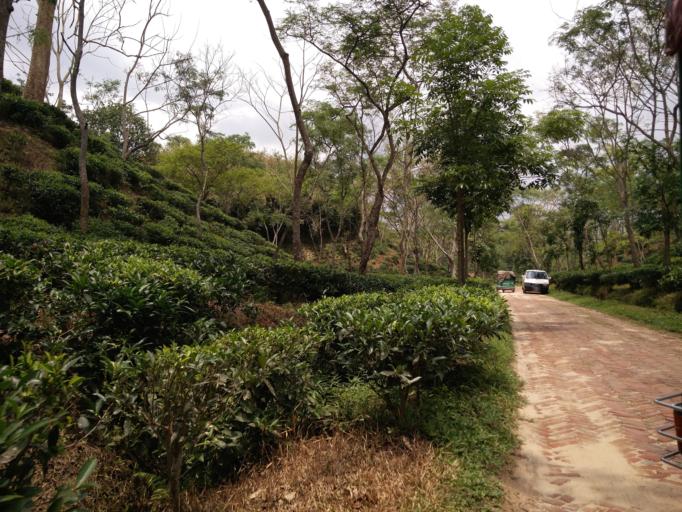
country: IN
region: Tripura
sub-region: Dhalai
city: Kamalpur
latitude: 24.3047
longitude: 91.8009
